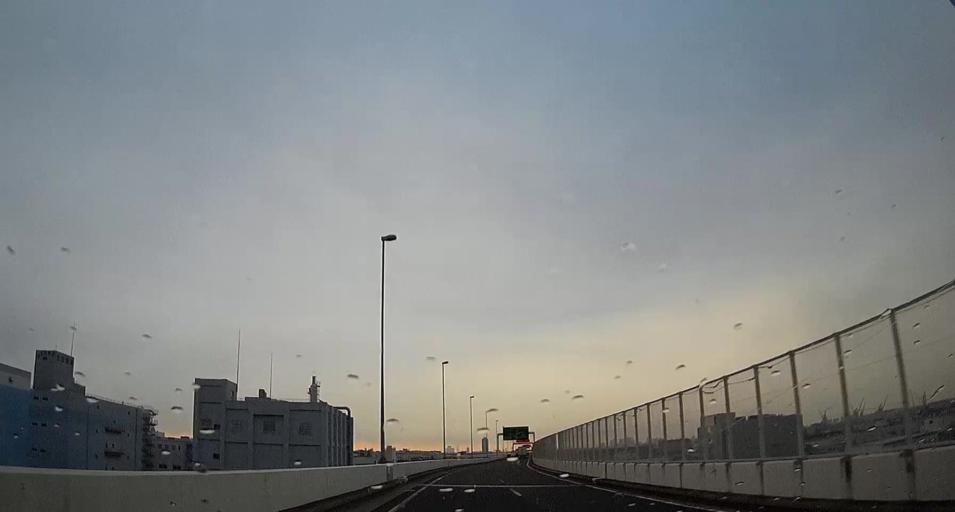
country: JP
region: Kanagawa
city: Yokohama
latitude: 35.4776
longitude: 139.6747
